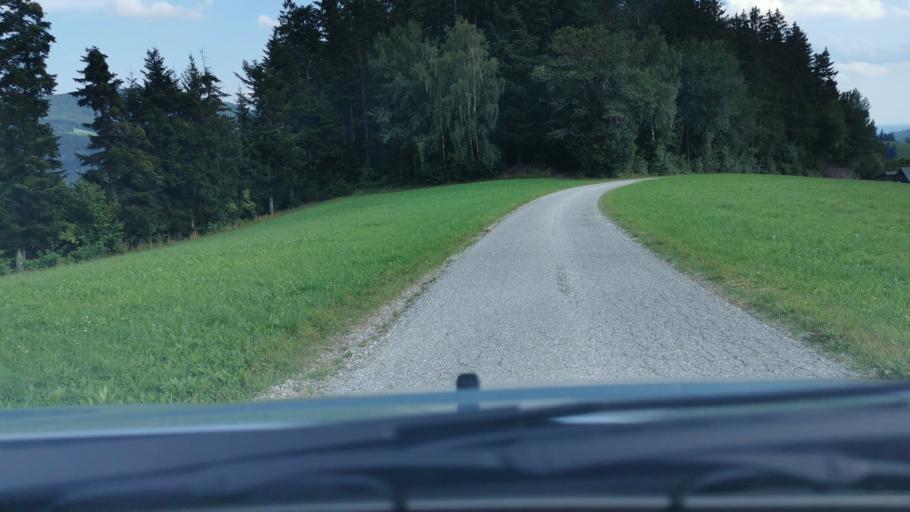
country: AT
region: Styria
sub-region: Politischer Bezirk Weiz
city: Koglhof
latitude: 47.3199
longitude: 15.6705
